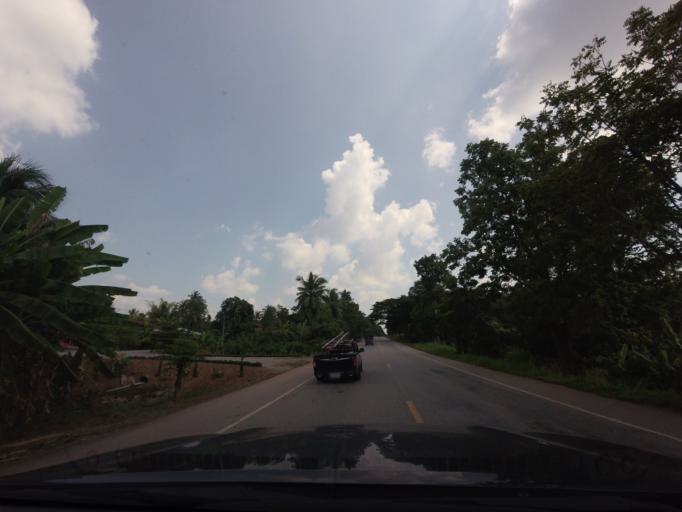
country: TH
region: Phitsanulok
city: Chat Trakan
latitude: 17.2803
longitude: 100.5370
